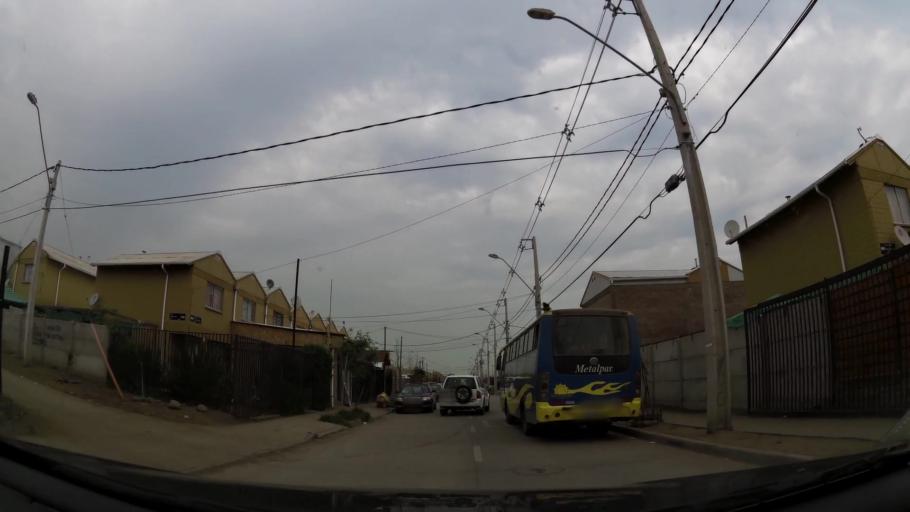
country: CL
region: Santiago Metropolitan
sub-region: Provincia de Chacabuco
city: Chicureo Abajo
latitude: -33.1834
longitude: -70.6655
